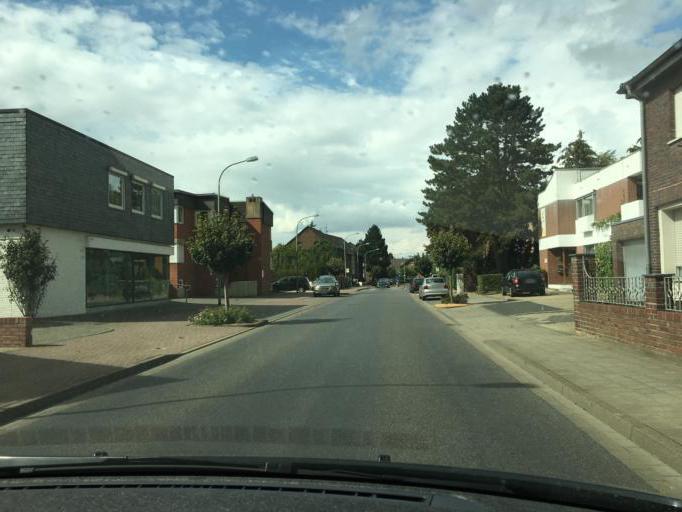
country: DE
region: North Rhine-Westphalia
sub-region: Regierungsbezirk Koln
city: Niederzier
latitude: 50.8797
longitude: 6.4678
